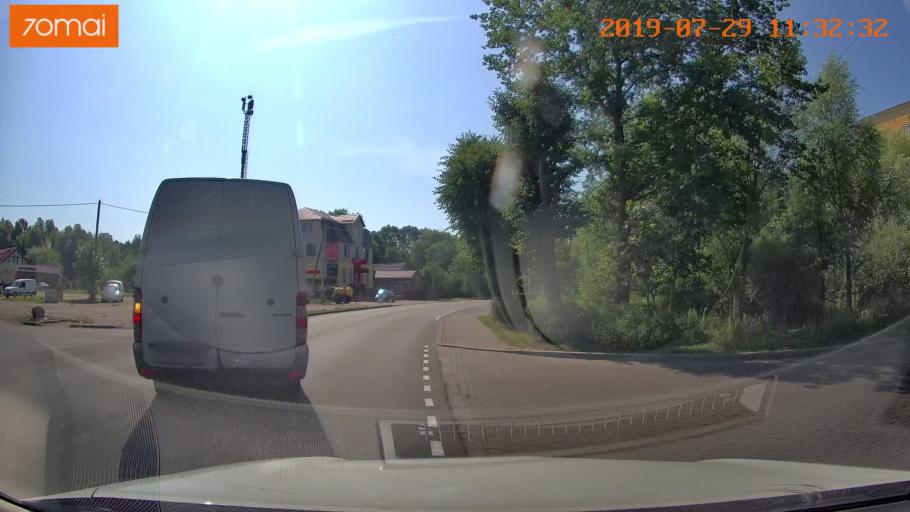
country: RU
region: Kaliningrad
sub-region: Gorod Kaliningrad
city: Kaliningrad
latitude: 54.6714
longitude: 20.5452
